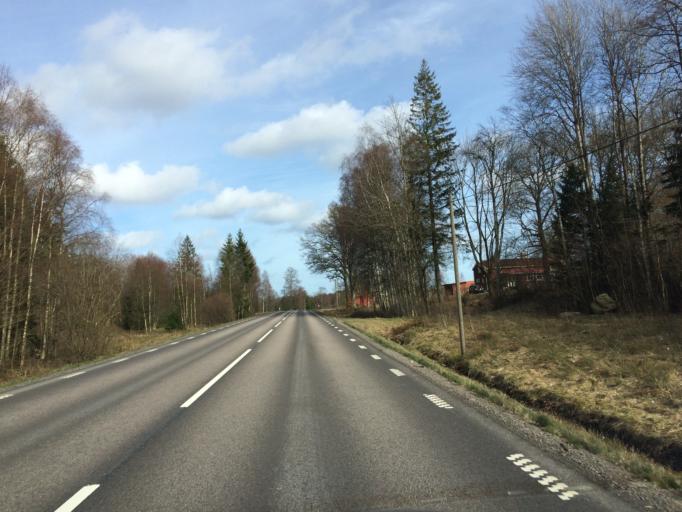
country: SE
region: Halland
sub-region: Hylte Kommun
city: Hyltebruk
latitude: 57.0249
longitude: 13.2177
